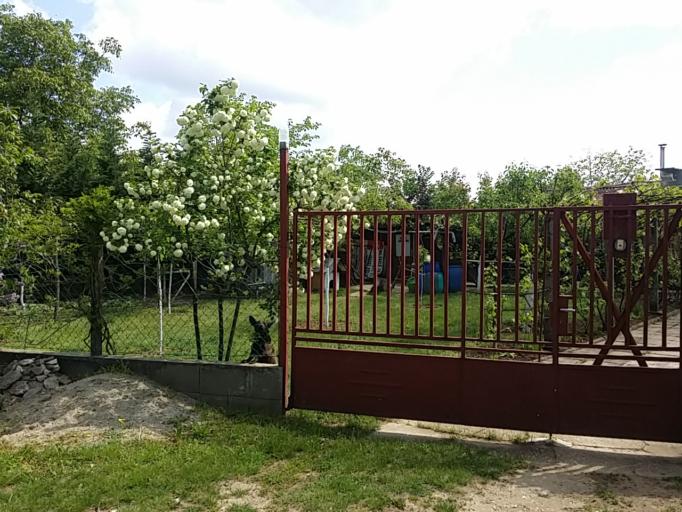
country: HU
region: Pest
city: Erdokertes
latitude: 47.6616
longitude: 19.3201
